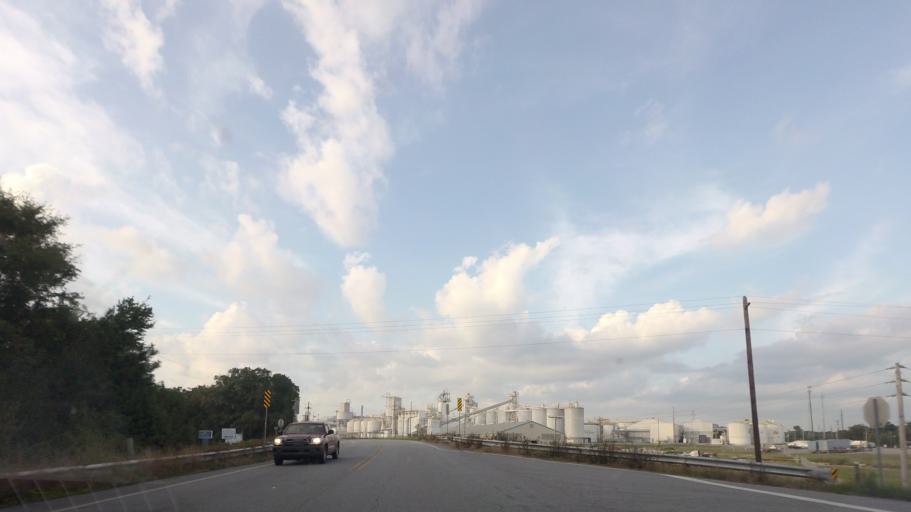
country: US
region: Georgia
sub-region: Wilkinson County
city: Gordon
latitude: 32.8776
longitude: -83.3398
